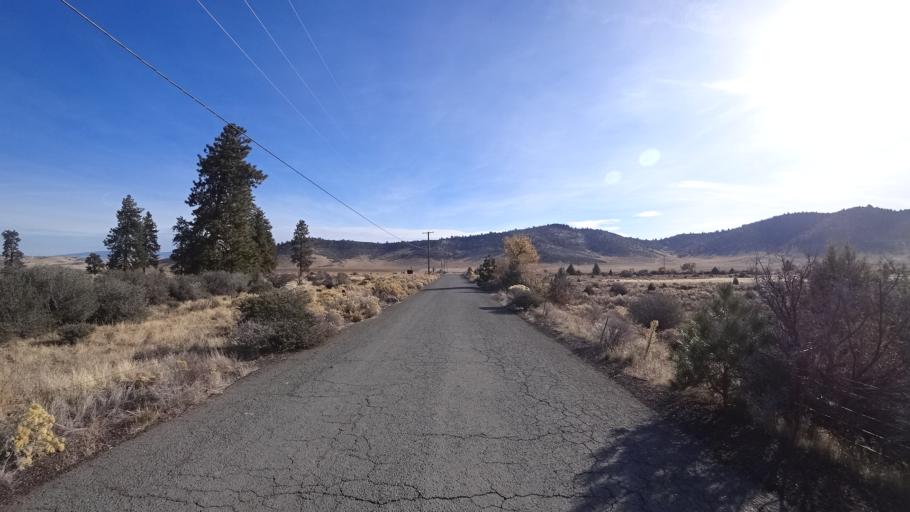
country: US
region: California
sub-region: Siskiyou County
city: Montague
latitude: 41.6363
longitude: -122.5714
